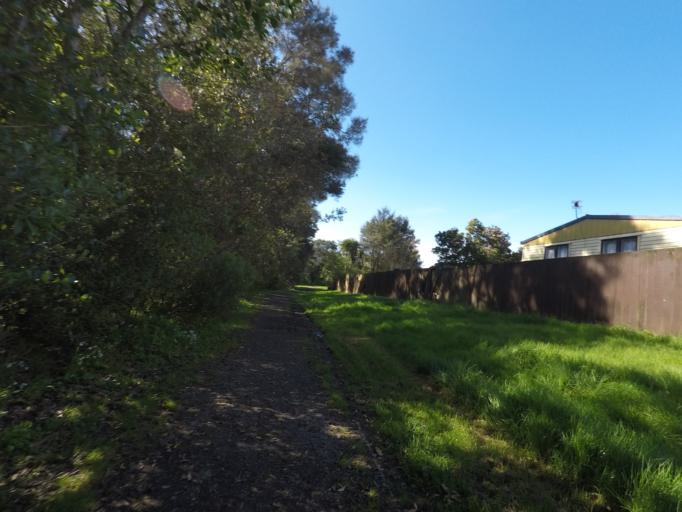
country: NZ
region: Auckland
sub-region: Auckland
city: Rosebank
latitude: -36.8582
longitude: 174.5981
